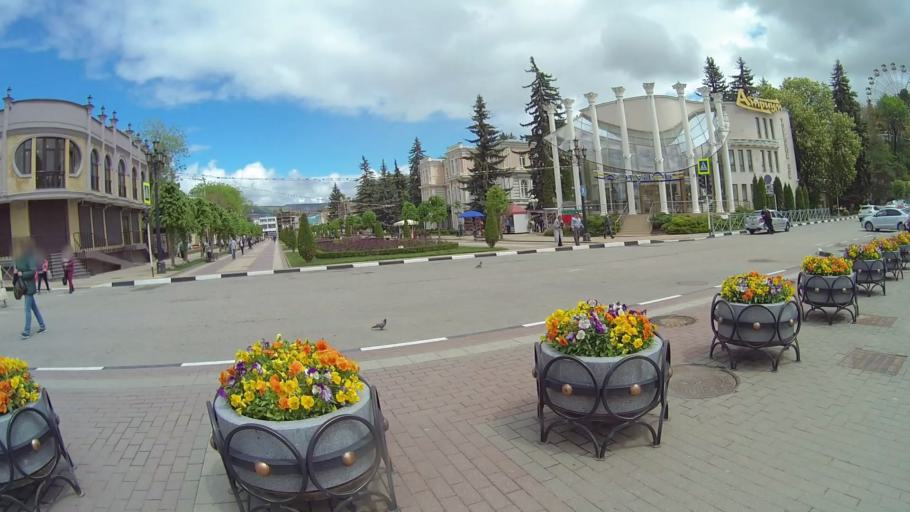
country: RU
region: Stavropol'skiy
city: Kislovodsk
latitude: 43.9028
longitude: 42.7168
